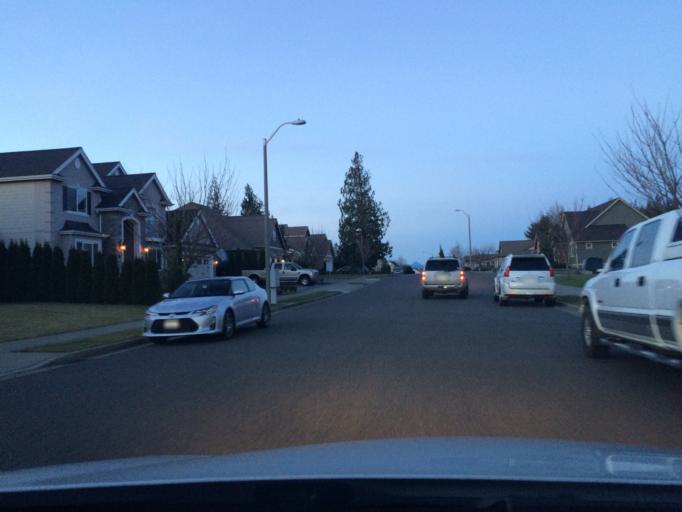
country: US
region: Washington
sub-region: Whatcom County
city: Lynden
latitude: 48.9549
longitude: -122.4251
